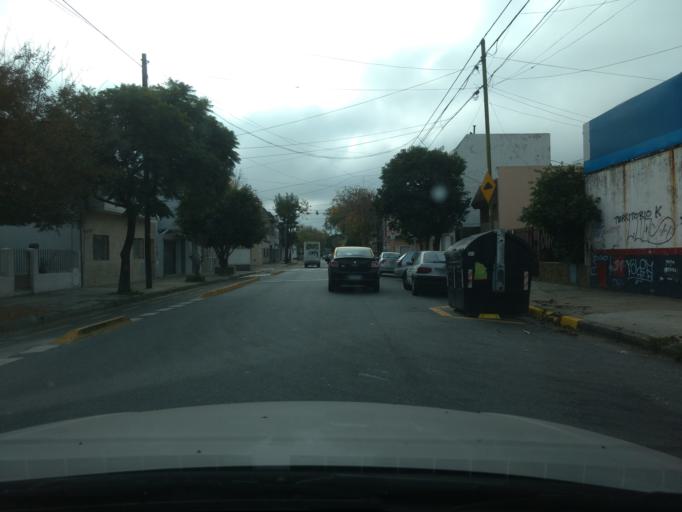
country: AR
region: Buenos Aires F.D.
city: Villa Santa Rita
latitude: -34.6159
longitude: -58.5091
